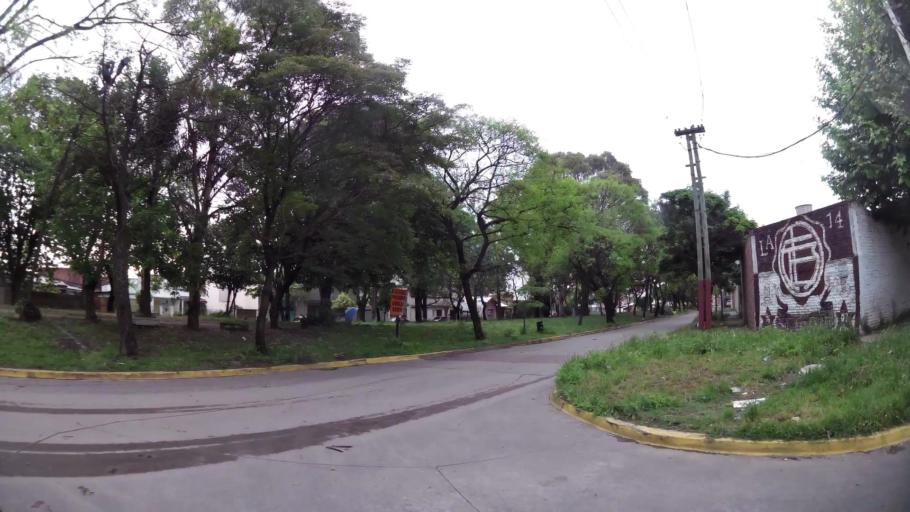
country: AR
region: Buenos Aires
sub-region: Partido de Lanus
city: Lanus
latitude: -34.7139
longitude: -58.3564
